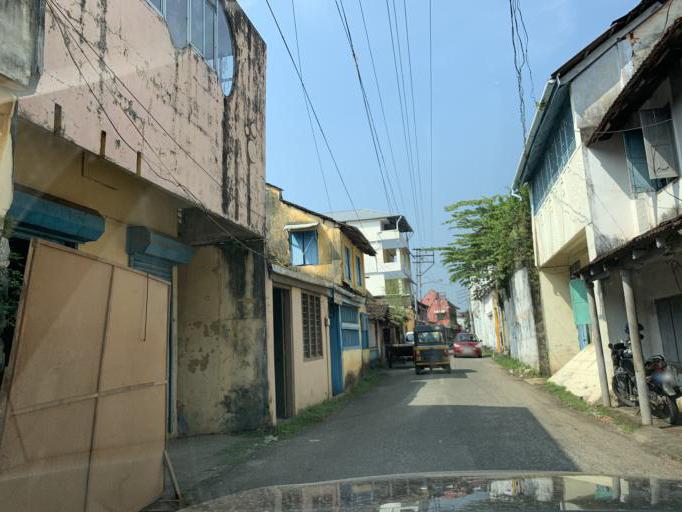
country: IN
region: Kerala
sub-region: Ernakulam
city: Cochin
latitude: 9.9543
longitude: 76.2603
